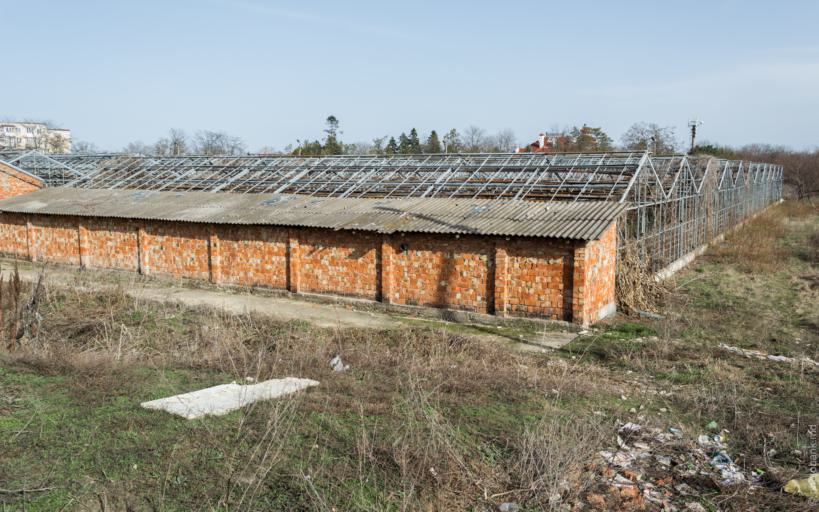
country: MD
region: Balti
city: Balti
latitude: 47.7670
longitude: 27.8933
